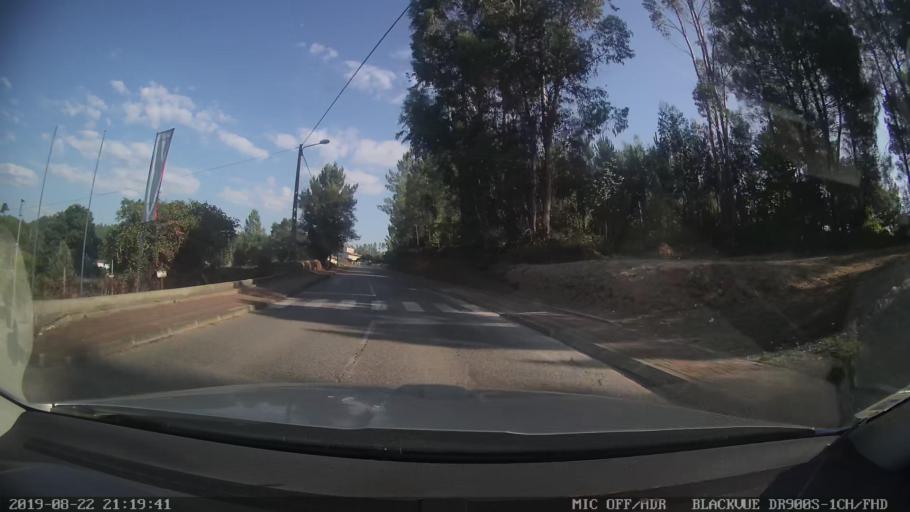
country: PT
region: Castelo Branco
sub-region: Serta
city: Serta
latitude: 39.8077
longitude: -8.1078
